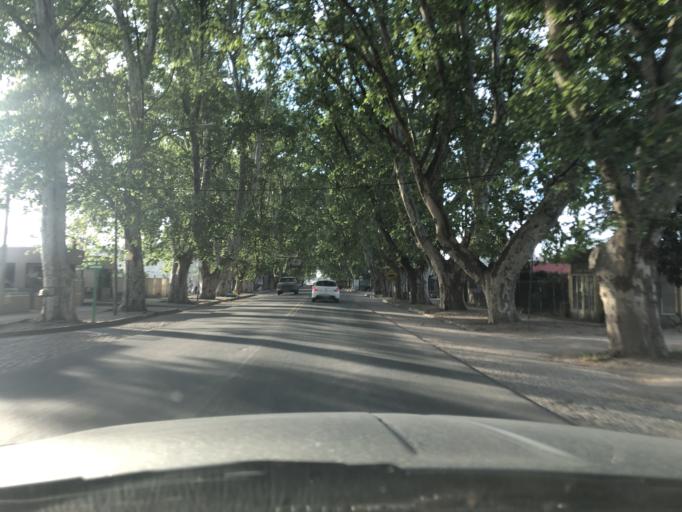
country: AR
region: Cordoba
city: Jesus Maria
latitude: -30.9927
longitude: -64.0951
